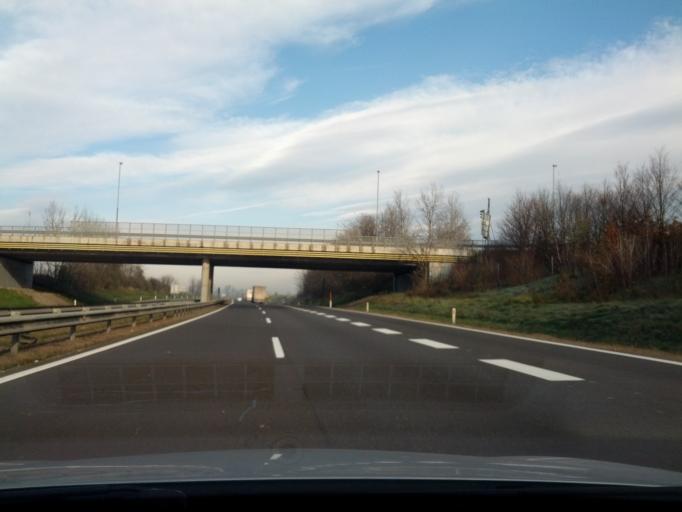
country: SI
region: Hoce-Slivnica
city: Rogoza
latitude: 46.4994
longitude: 15.6703
